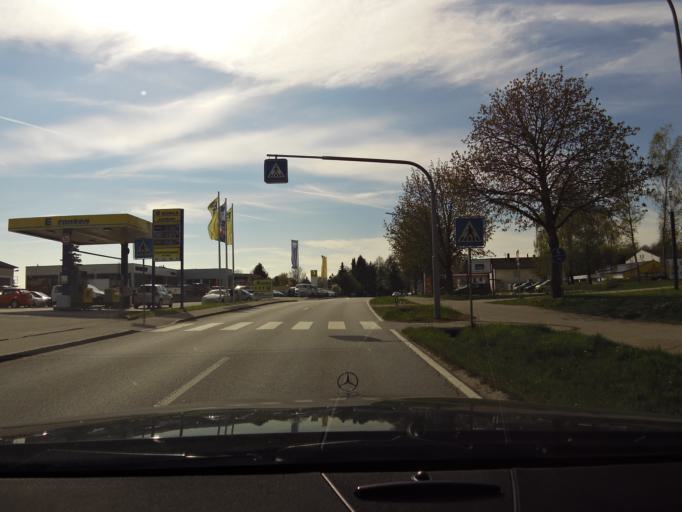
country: DE
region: Bavaria
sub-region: Lower Bavaria
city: Mallersdorf-Pfaffenberg
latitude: 48.7709
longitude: 12.2362
